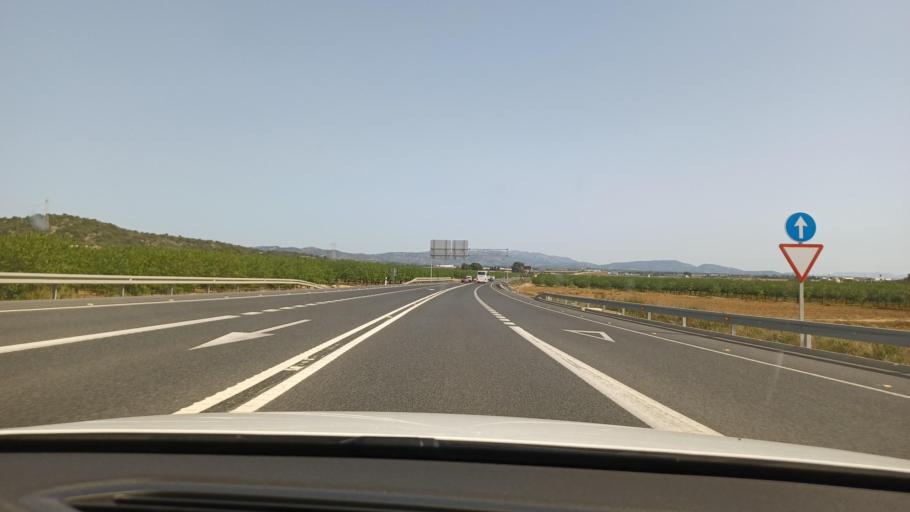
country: ES
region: Catalonia
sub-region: Provincia de Tarragona
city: Amposta
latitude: 40.7322
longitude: 0.5910
